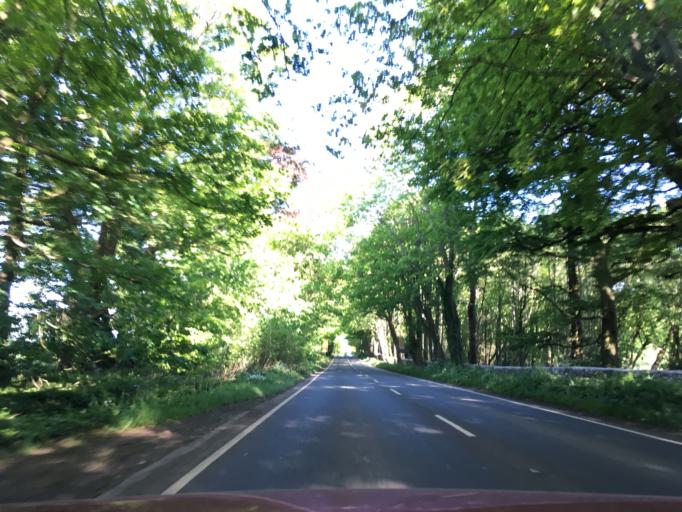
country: GB
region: England
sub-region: North Somerset
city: Easton-in-Gordano
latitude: 51.4489
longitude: -2.7226
